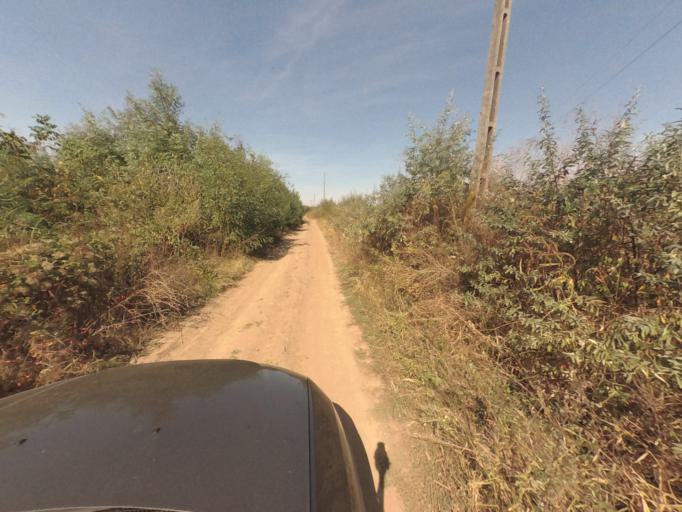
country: RO
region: Vaslui
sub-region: Comuna Costesti
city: Costesti
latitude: 46.5148
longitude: 27.7434
